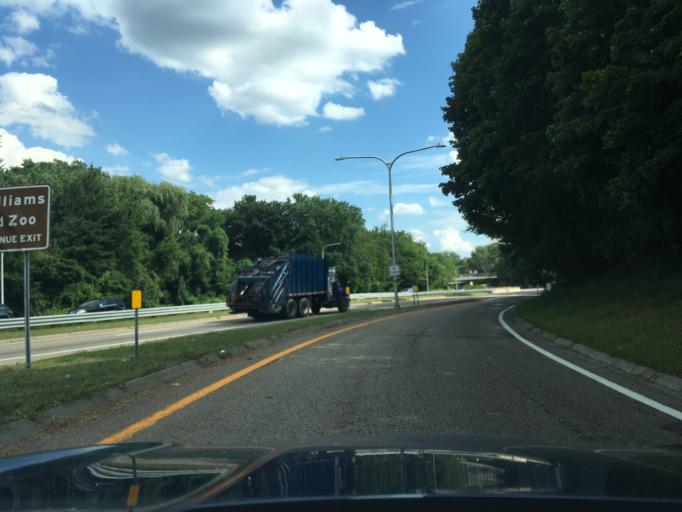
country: US
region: Rhode Island
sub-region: Providence County
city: Cranston
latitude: 41.7849
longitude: -71.4329
